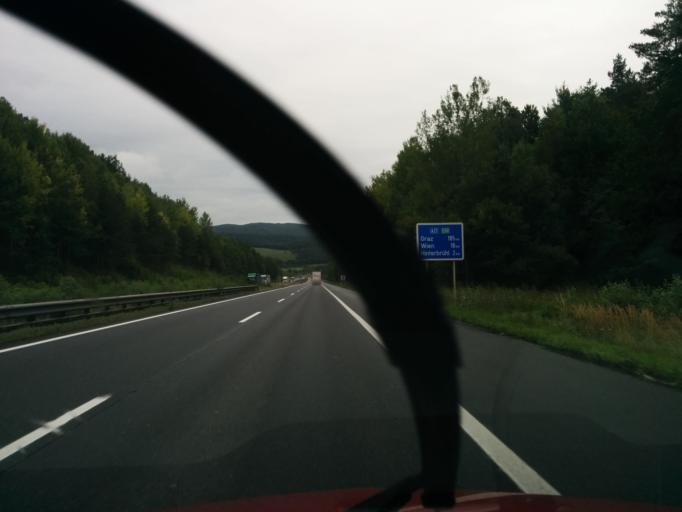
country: AT
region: Lower Austria
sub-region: Politischer Bezirk Modling
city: Gaaden
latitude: 48.0633
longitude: 16.1648
